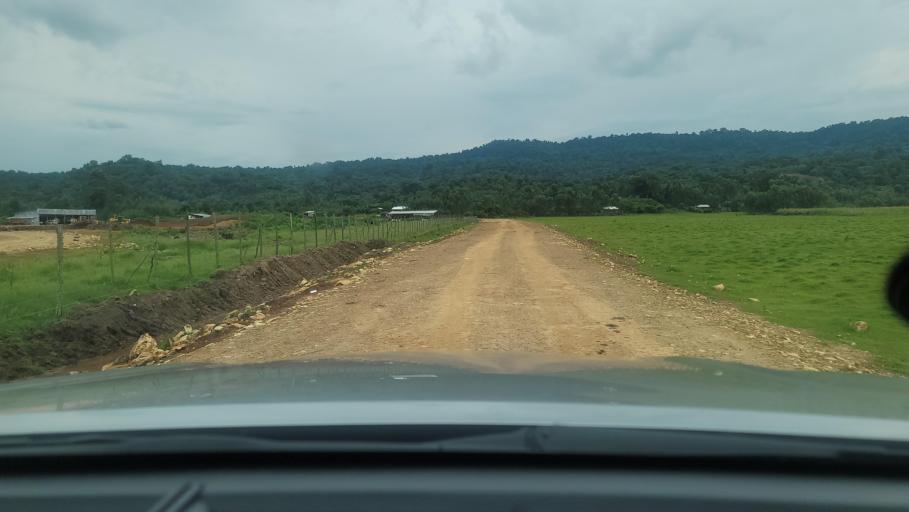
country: ET
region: Oromiya
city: Agaro
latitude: 7.7637
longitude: 36.3160
